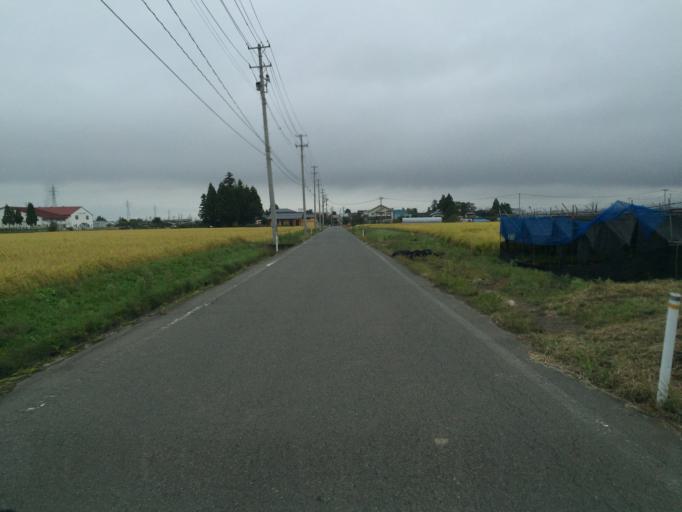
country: JP
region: Fukushima
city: Kitakata
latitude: 37.4650
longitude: 139.9148
